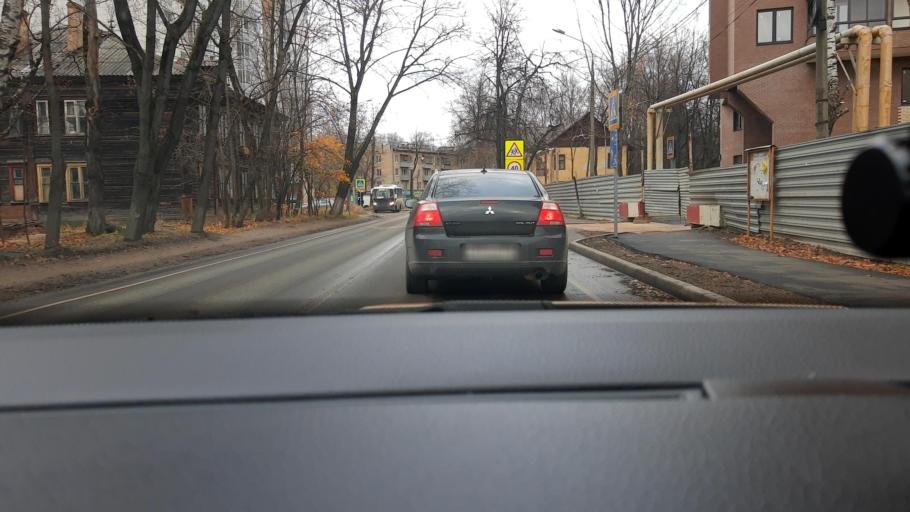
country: RU
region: Moskovskaya
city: Krasnogorsk
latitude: 55.8335
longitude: 37.3120
